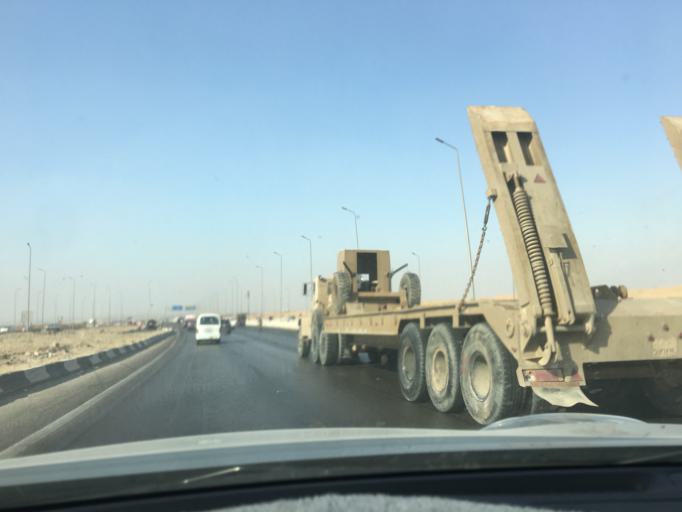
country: EG
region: Muhafazat al Qalyubiyah
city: Al Khankah
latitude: 30.1177
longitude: 31.4605
